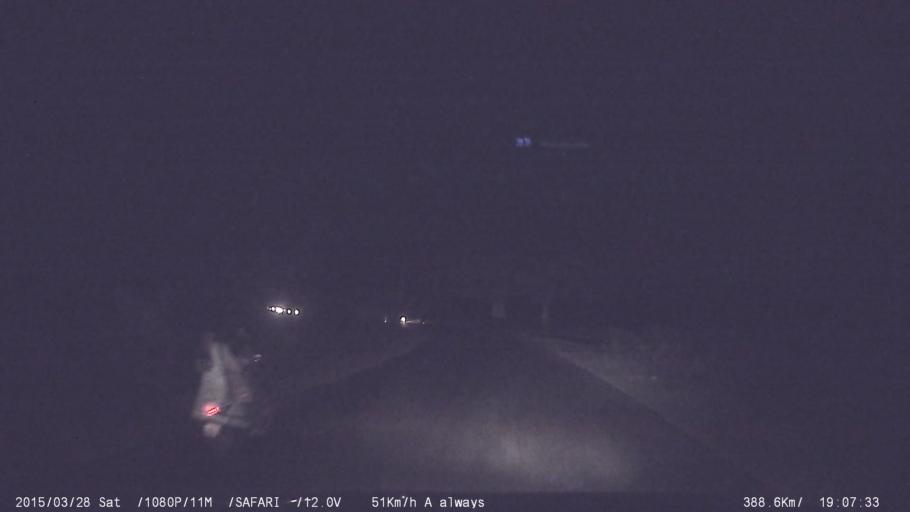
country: IN
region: Karnataka
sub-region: Mandya
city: Shrirangapattana
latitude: 12.3921
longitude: 76.6155
